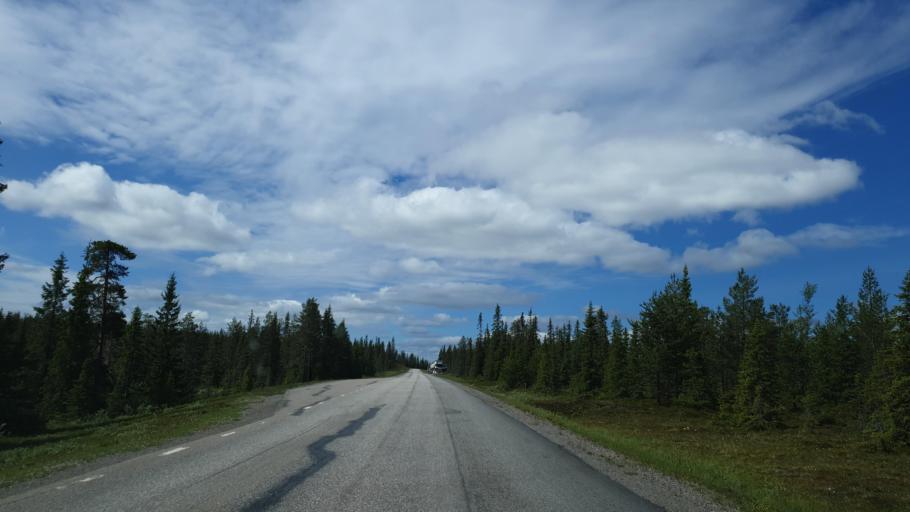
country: SE
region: Vaesterbotten
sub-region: Mala Kommun
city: Mala
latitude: 65.5713
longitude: 18.3711
